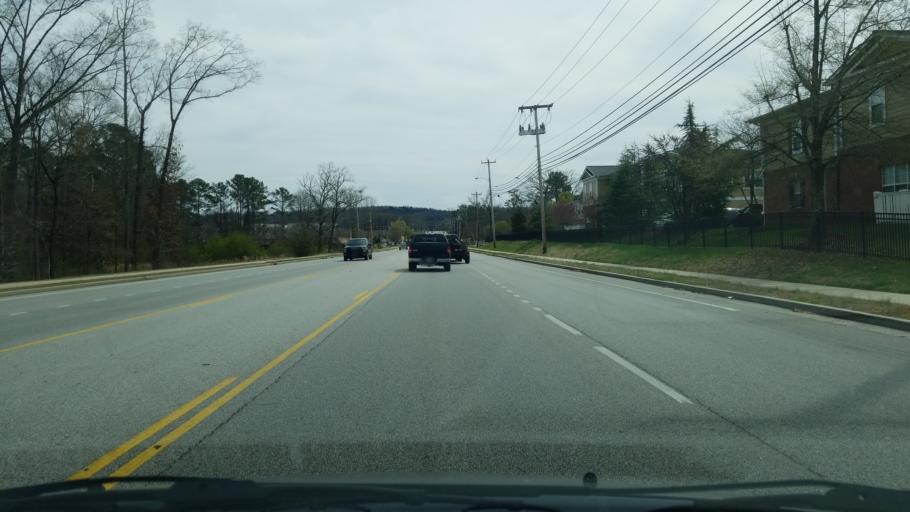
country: US
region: Tennessee
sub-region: Hamilton County
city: East Brainerd
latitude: 35.0380
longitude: -85.1434
